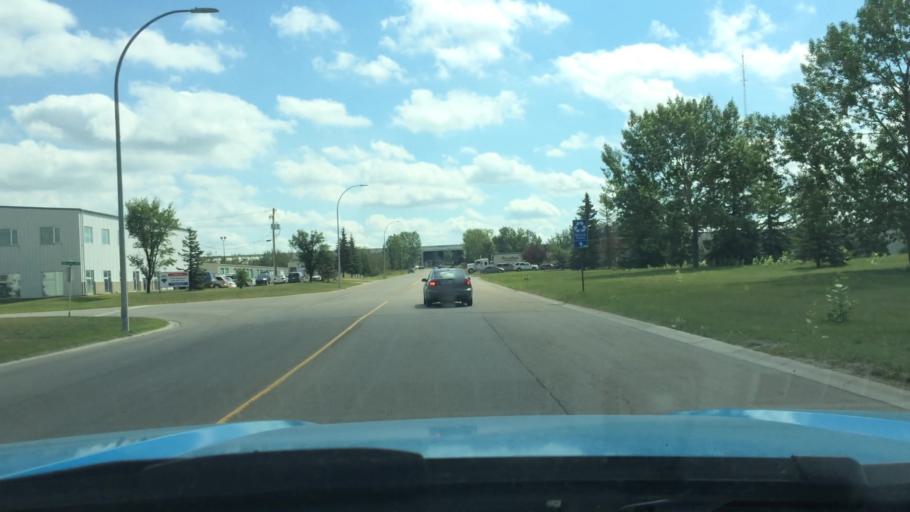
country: CA
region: Alberta
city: Airdrie
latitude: 51.2889
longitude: -113.9884
